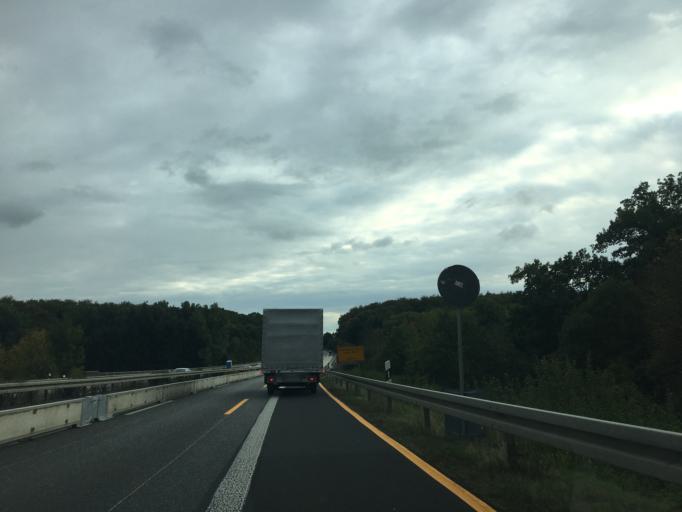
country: DE
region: Hesse
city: Staufenberg
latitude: 50.6798
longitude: 8.7203
